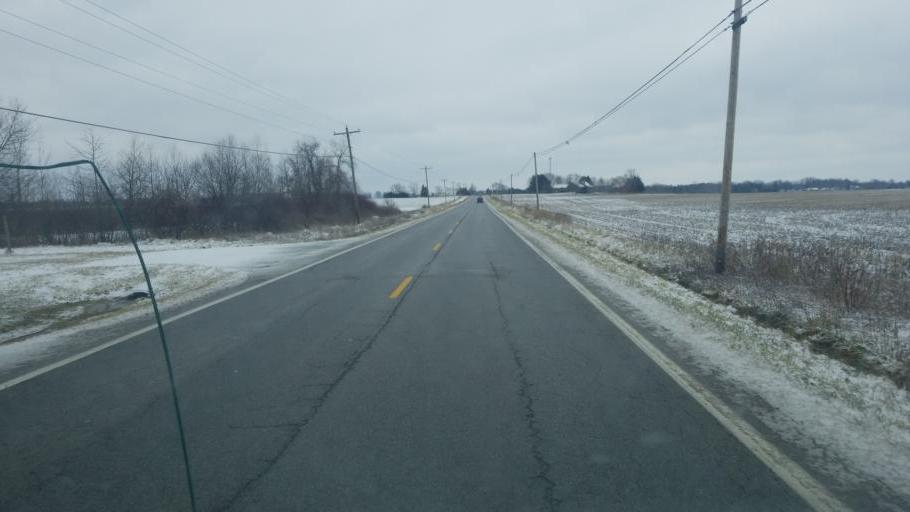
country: US
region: Ohio
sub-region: Licking County
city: Johnstown
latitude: 40.1943
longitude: -82.7636
